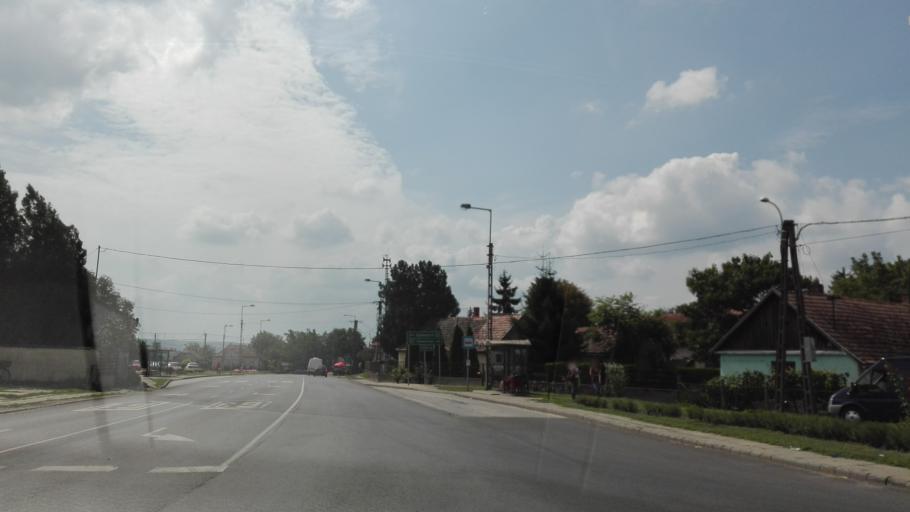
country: HU
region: Fejer
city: Cece
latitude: 46.7713
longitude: 18.6298
